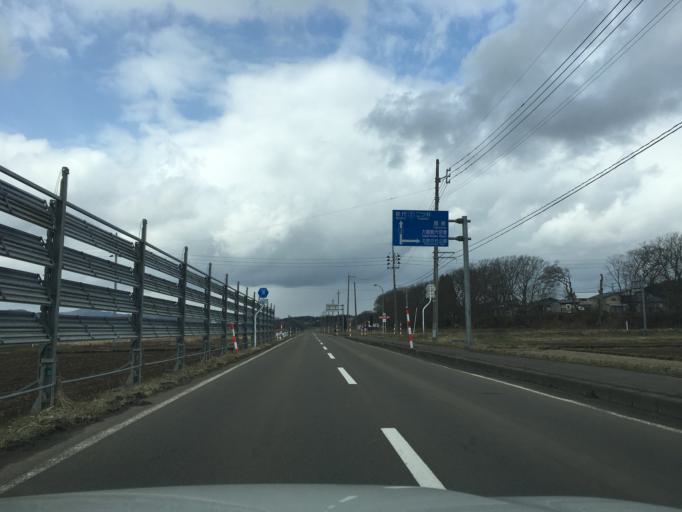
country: JP
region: Akita
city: Takanosu
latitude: 40.1488
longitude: 140.3404
